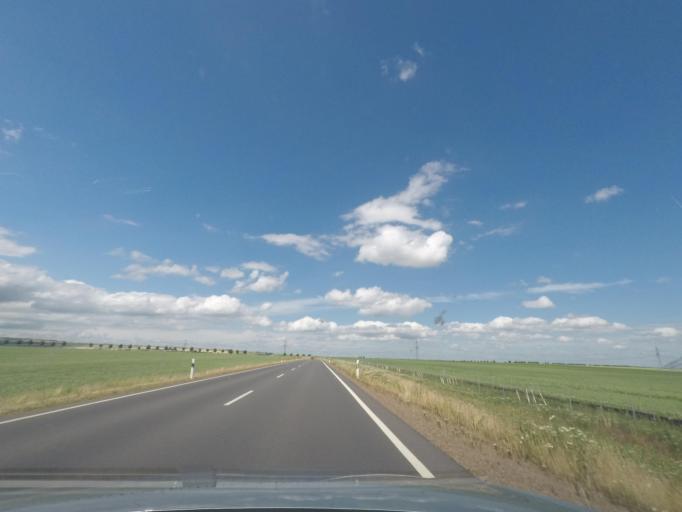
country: DE
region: Saxony-Anhalt
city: Gross Quenstedt
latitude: 51.9040
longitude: 11.1116
